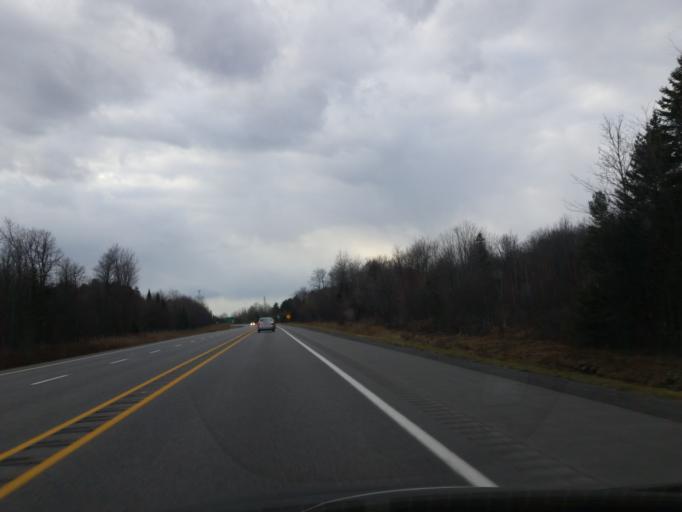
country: CA
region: Quebec
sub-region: Laurentides
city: Saint-Colomban
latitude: 45.6798
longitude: -74.1648
